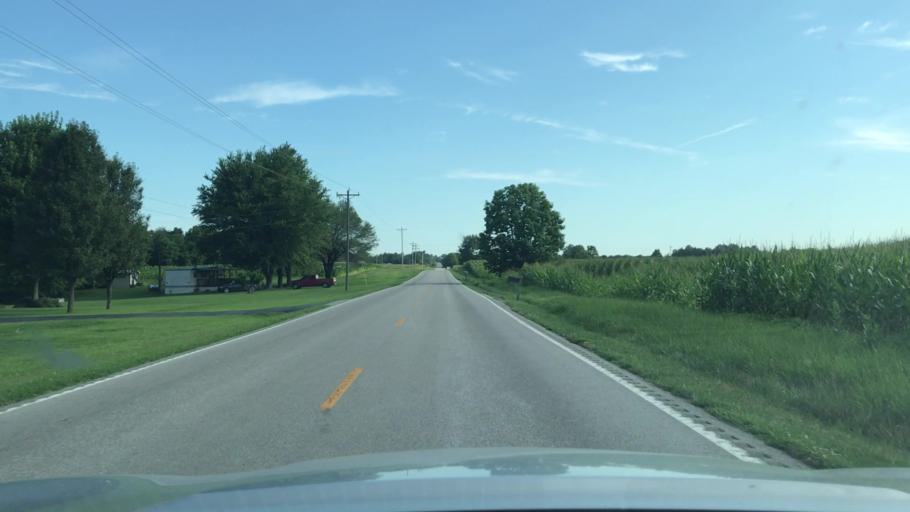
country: US
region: Kentucky
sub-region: Todd County
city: Elkton
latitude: 36.9168
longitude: -87.1630
